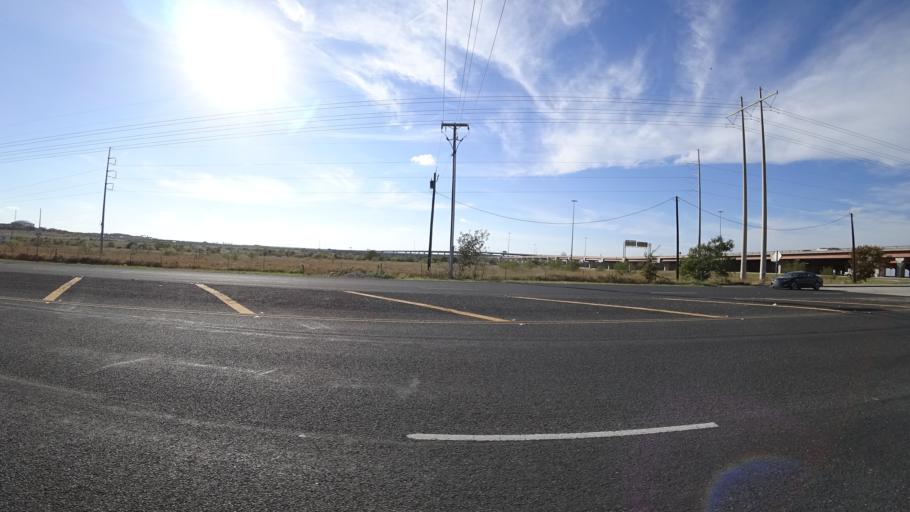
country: US
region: Texas
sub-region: Travis County
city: Wells Branch
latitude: 30.4765
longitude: -97.6936
